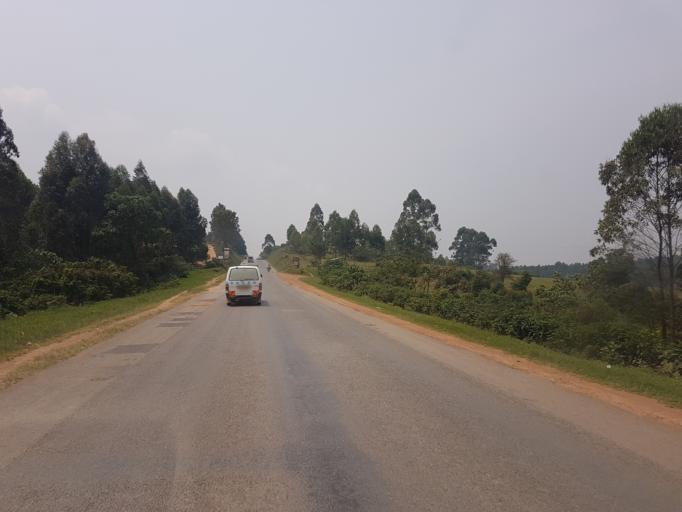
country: UG
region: Western Region
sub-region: Bushenyi District
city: Bushenyi
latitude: -0.5413
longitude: 30.1740
